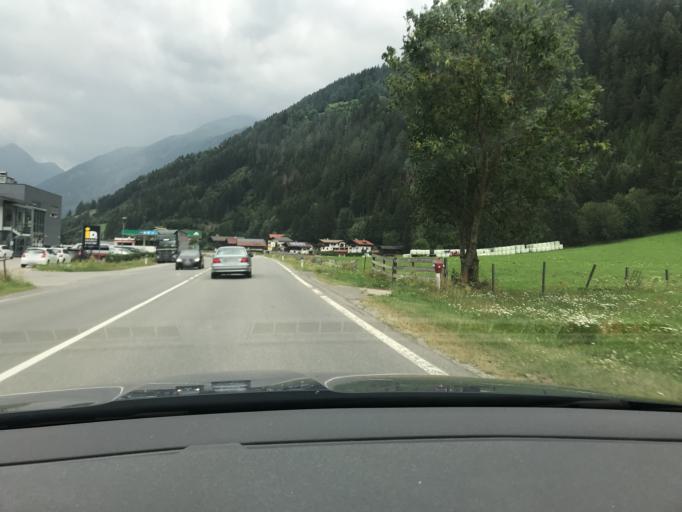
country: AT
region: Tyrol
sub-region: Politischer Bezirk Lienz
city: Matrei in Osttirol
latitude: 46.9799
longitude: 12.5503
